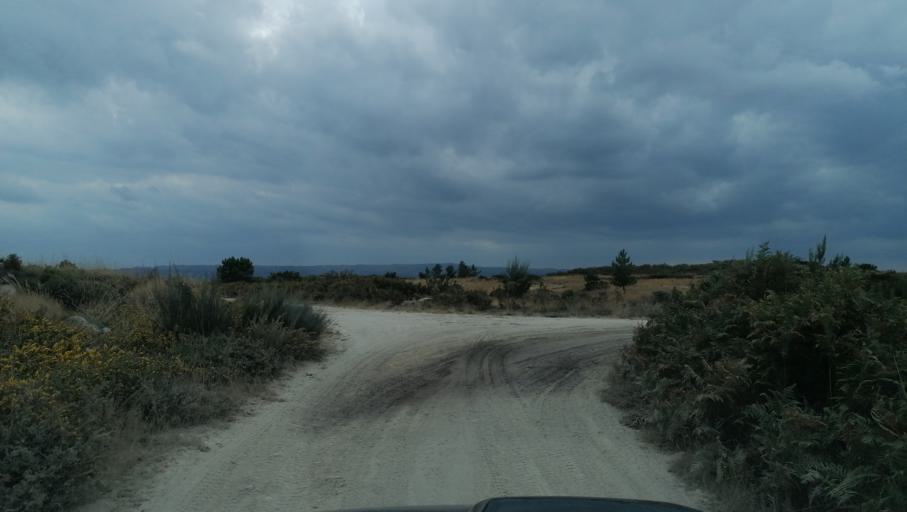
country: PT
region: Vila Real
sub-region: Vila Pouca de Aguiar
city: Vila Pouca de Aguiar
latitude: 41.5346
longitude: -7.6943
